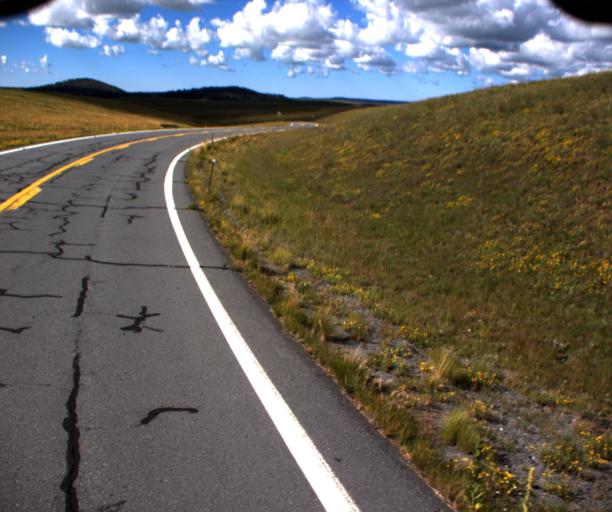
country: US
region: Arizona
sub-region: Apache County
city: Eagar
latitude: 33.9574
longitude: -109.3940
